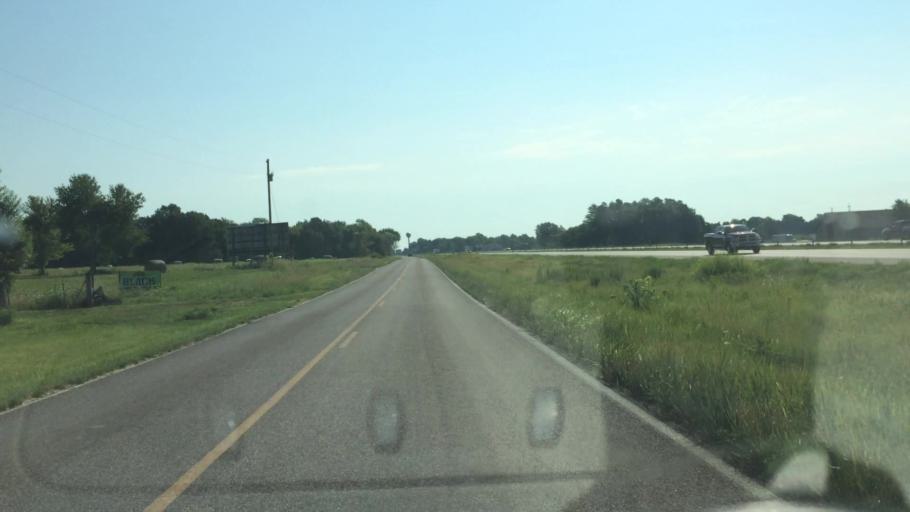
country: US
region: Missouri
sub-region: Greene County
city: Strafford
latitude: 37.2651
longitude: -93.1415
